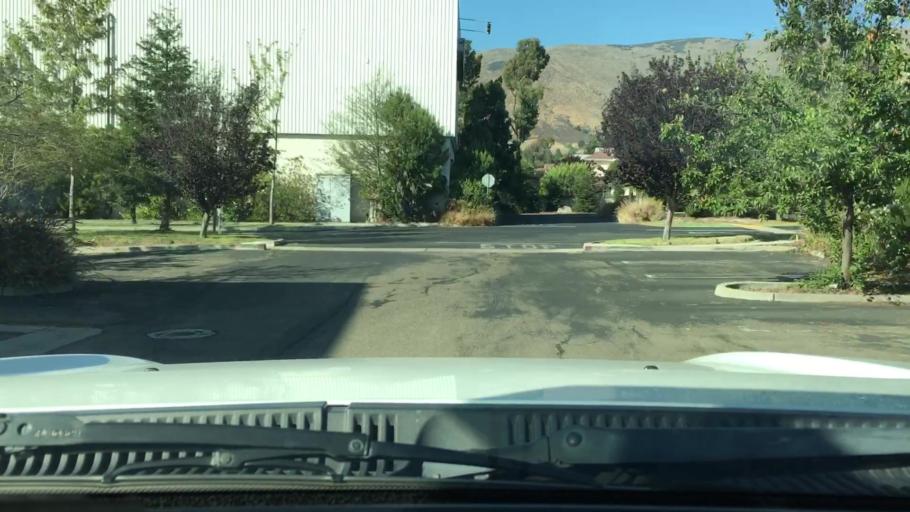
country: US
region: California
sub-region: San Luis Obispo County
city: San Luis Obispo
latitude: 35.2635
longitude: -120.6436
